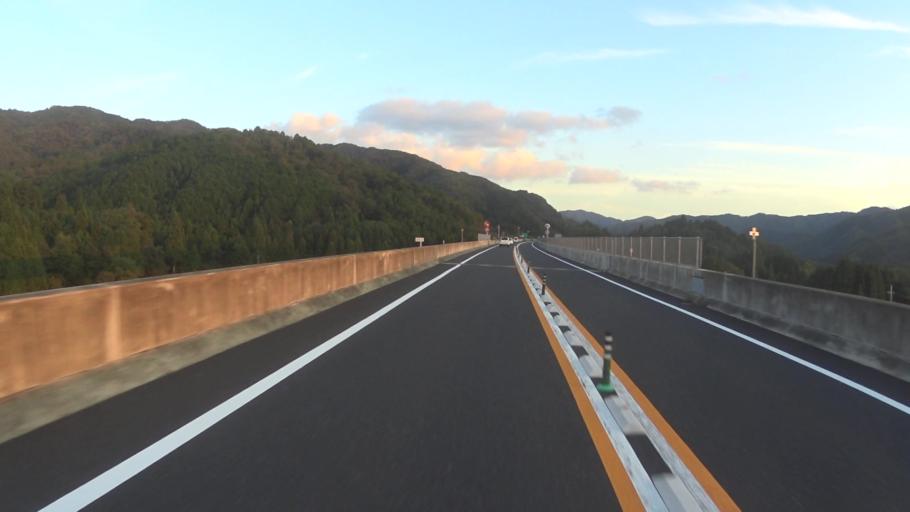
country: JP
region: Kyoto
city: Ayabe
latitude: 35.2962
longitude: 135.3337
